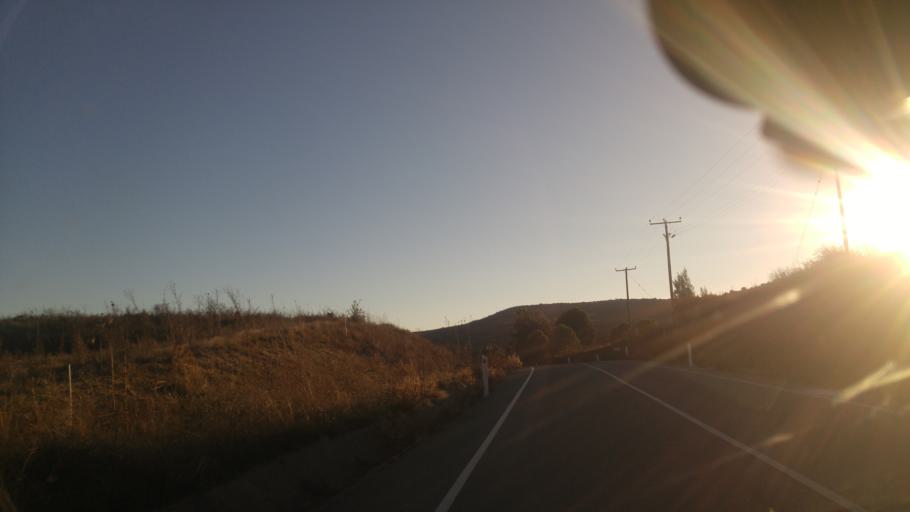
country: CY
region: Limassol
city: Pachna
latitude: 34.8567
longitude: 32.8068
